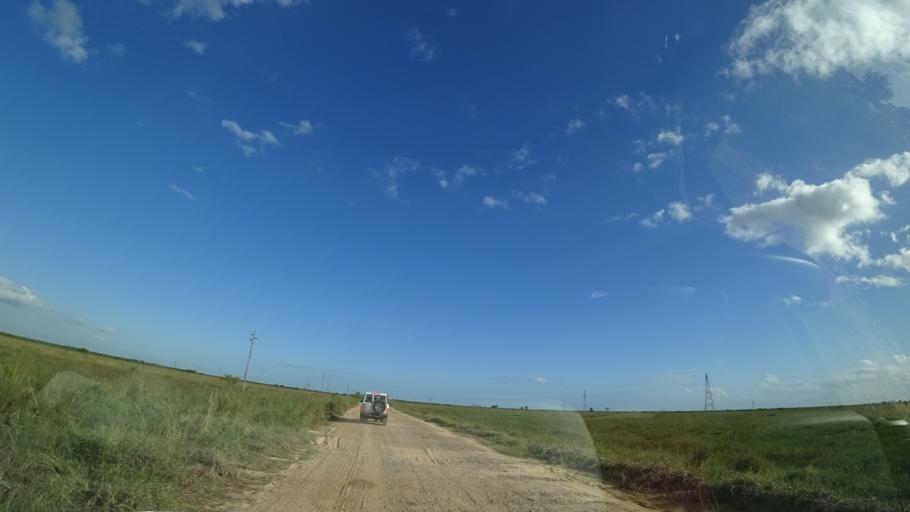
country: MZ
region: Sofala
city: Dondo
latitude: -19.4556
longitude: 34.5629
